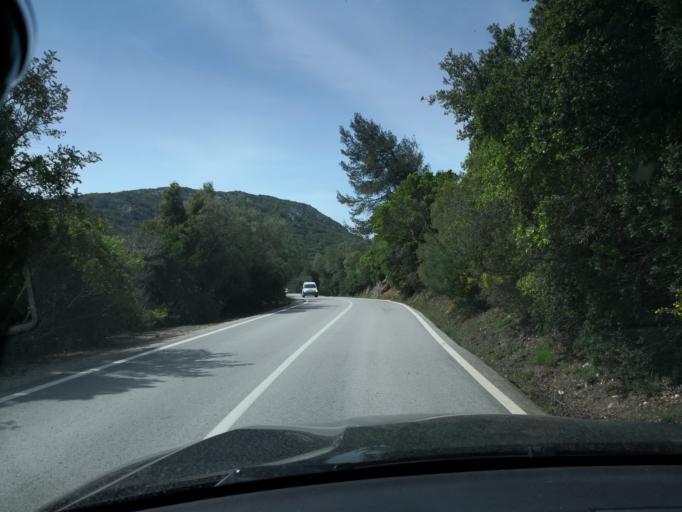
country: PT
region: Setubal
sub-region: Sesimbra
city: Sesimbra
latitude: 38.4684
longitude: -8.9948
